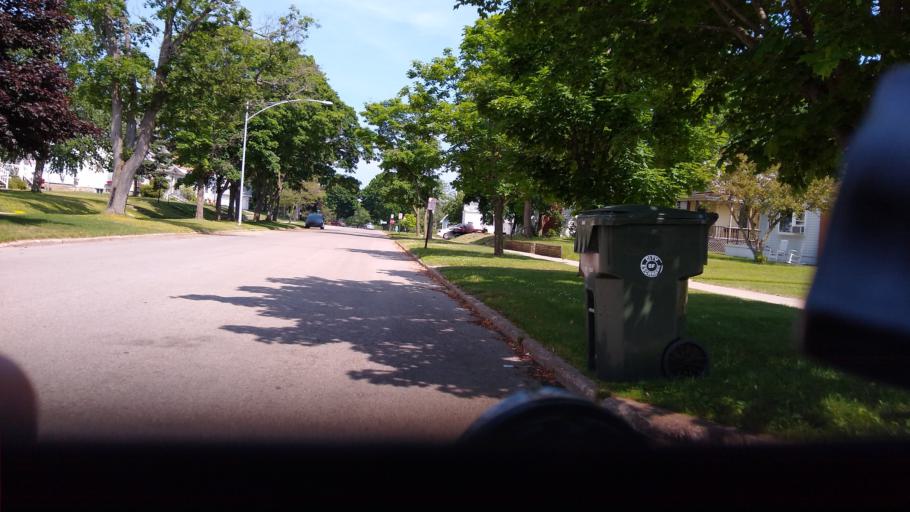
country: US
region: Michigan
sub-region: Delta County
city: Escanaba
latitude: 45.7373
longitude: -87.0608
